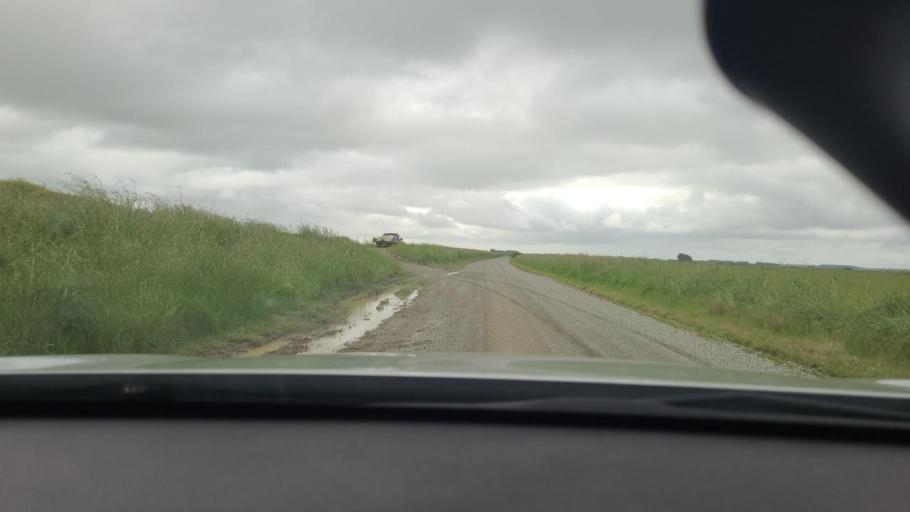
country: NZ
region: Southland
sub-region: Invercargill City
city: Invercargill
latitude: -46.3533
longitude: 168.2449
